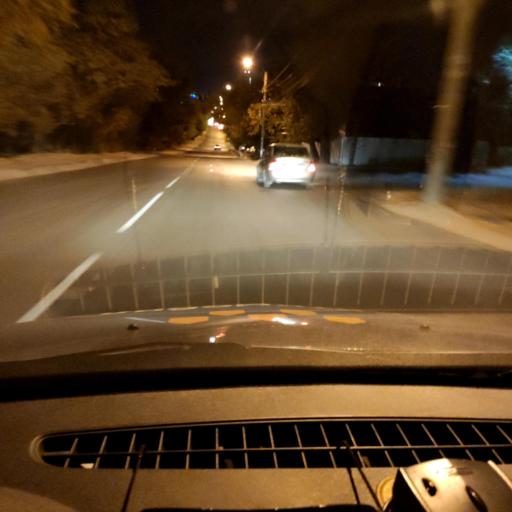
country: RU
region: Voronezj
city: Voronezh
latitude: 51.6918
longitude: 39.1648
